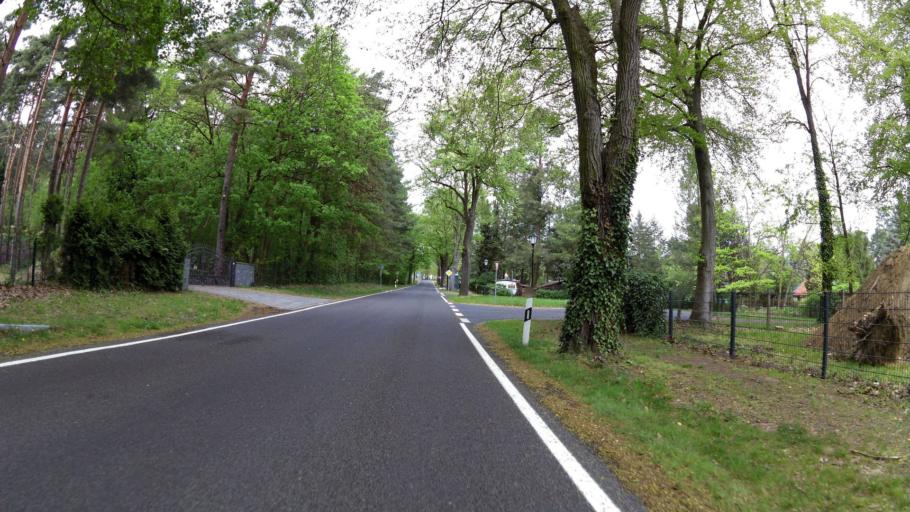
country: DE
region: Brandenburg
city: Mittenwalde
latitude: 52.2008
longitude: 13.5737
